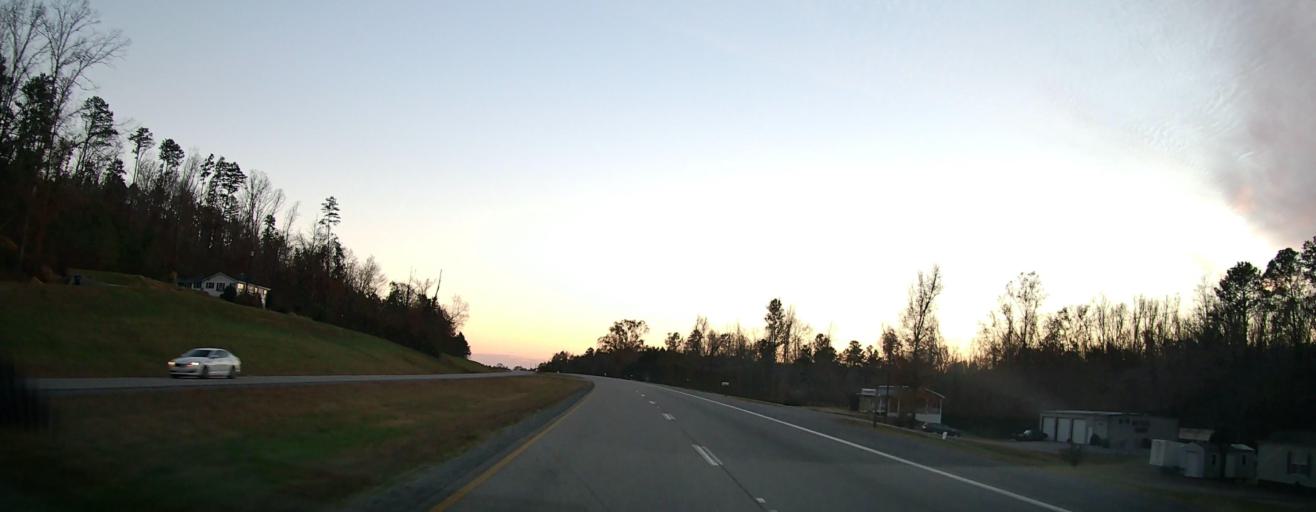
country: US
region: Alabama
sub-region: Calhoun County
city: Alexandria
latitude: 33.8445
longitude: -85.9160
